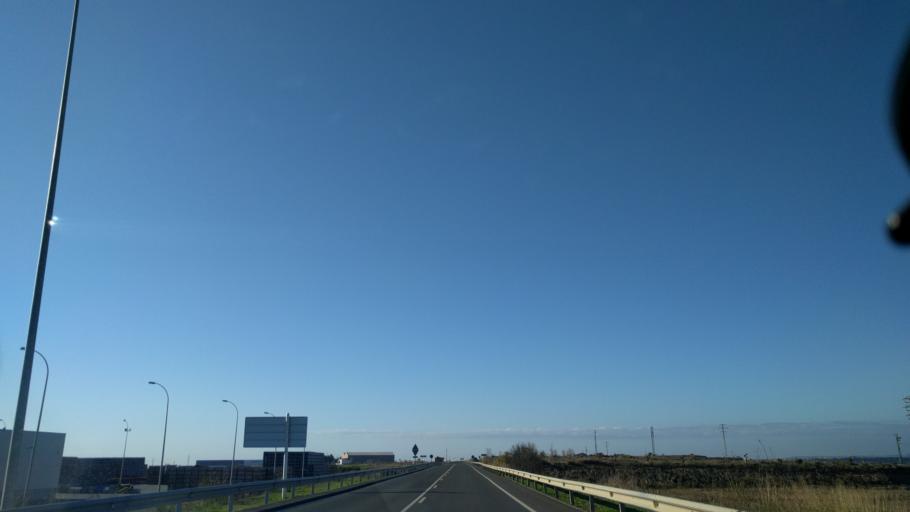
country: ES
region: Catalonia
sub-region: Provincia de Lleida
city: Termens
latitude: 41.7071
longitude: 0.7512
